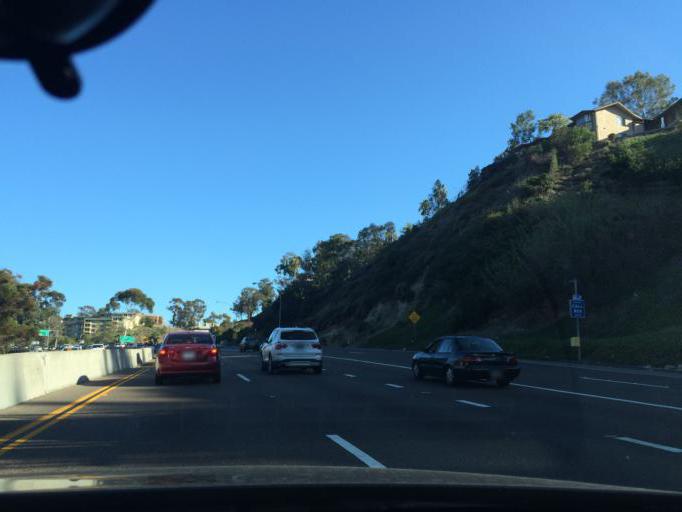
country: US
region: California
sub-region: San Diego County
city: San Diego
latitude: 32.7552
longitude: -117.1588
